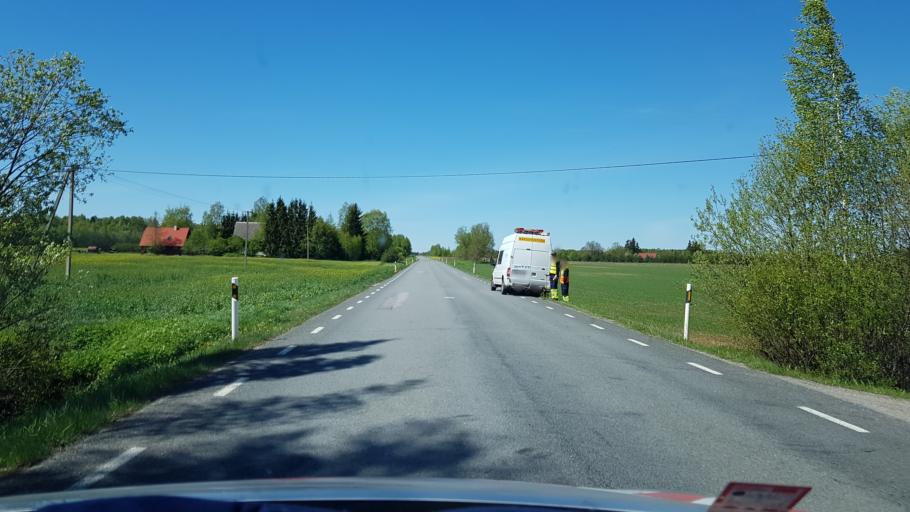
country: EE
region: Tartu
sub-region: UElenurme vald
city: Ulenurme
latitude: 58.3110
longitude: 26.6684
